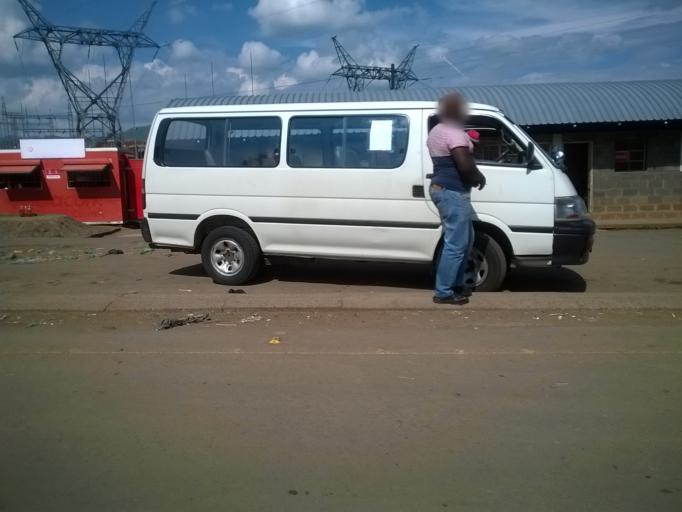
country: LS
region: Butha-Buthe
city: Butha-Buthe
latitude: -29.1089
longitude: 28.4913
